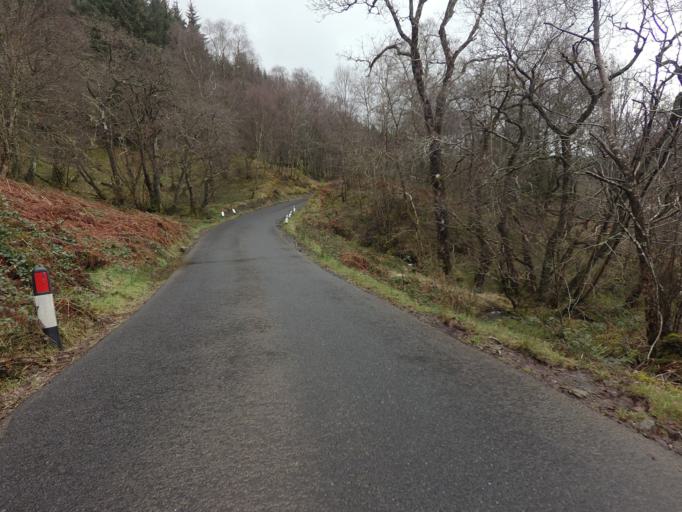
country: GB
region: Scotland
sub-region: West Dunbartonshire
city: Balloch
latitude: 56.2170
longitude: -4.5447
